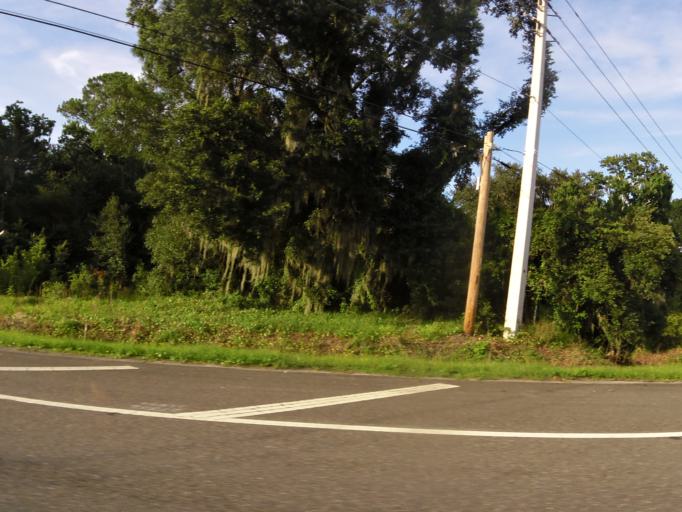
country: US
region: Florida
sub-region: Clay County
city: Green Cove Springs
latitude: 30.0142
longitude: -81.6046
